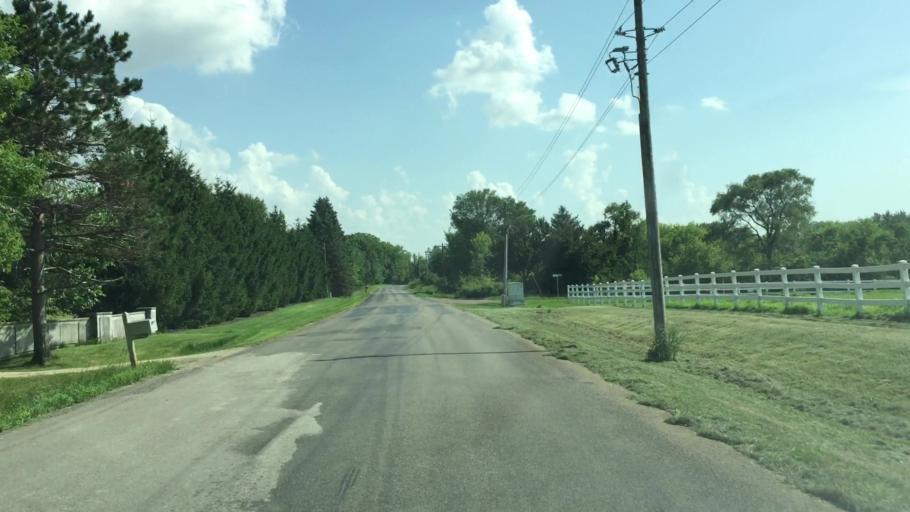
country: US
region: Iowa
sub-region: Johnson County
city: North Liberty
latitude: 41.8084
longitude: -91.6154
